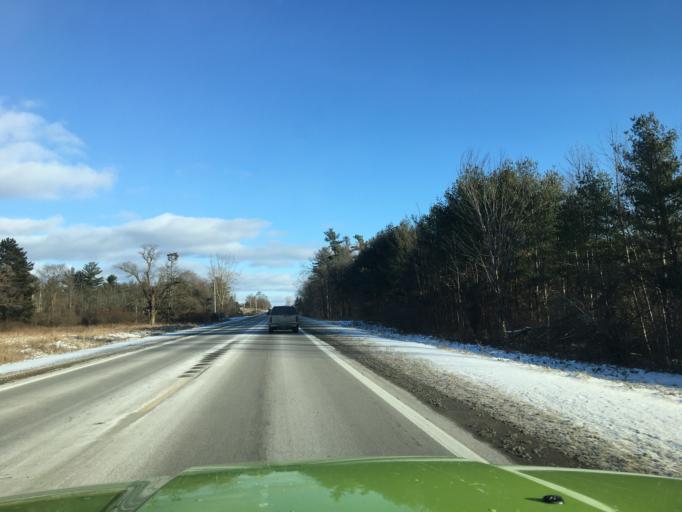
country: US
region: Michigan
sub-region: Kent County
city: Cedar Springs
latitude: 43.1755
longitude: -85.5200
